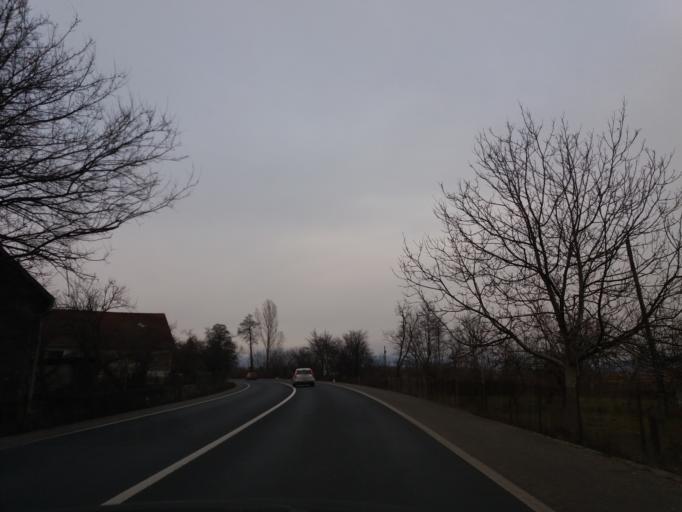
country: RO
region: Hunedoara
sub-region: Comuna Bacia
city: Bacia
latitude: 45.7875
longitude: 23.0016
